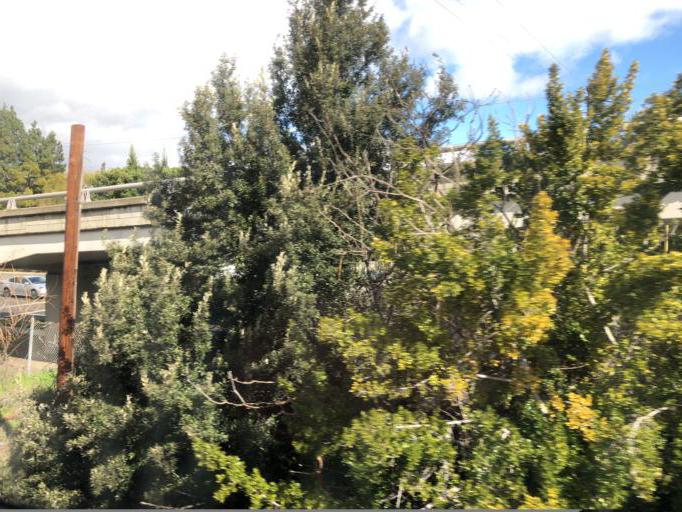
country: US
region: California
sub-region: Santa Clara County
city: Los Altos
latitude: 37.4084
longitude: -122.1088
